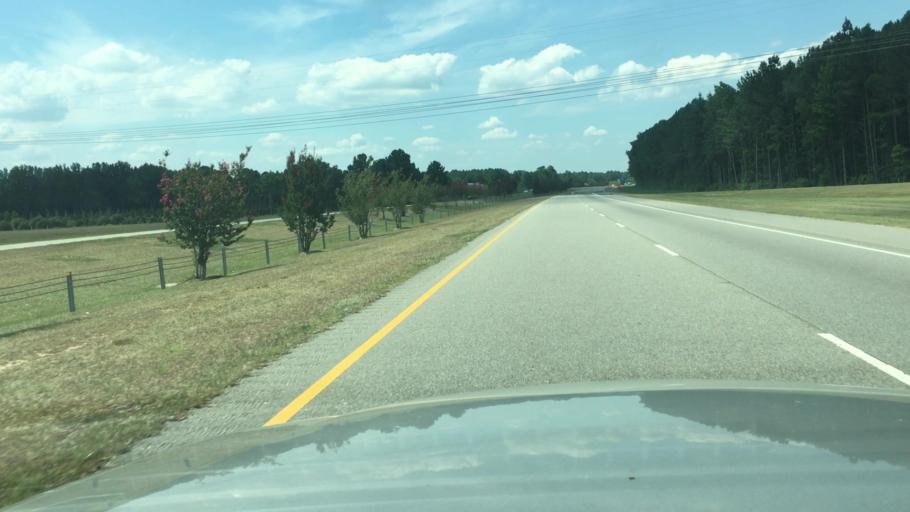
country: US
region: North Carolina
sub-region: Cumberland County
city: Fayetteville
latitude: 35.0113
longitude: -78.8693
